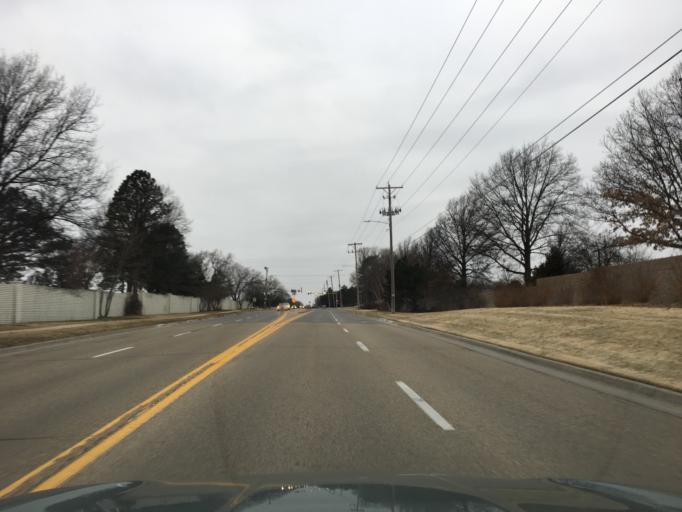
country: US
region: Kansas
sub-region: Sedgwick County
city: Bellaire
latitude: 37.7085
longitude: -97.2419
